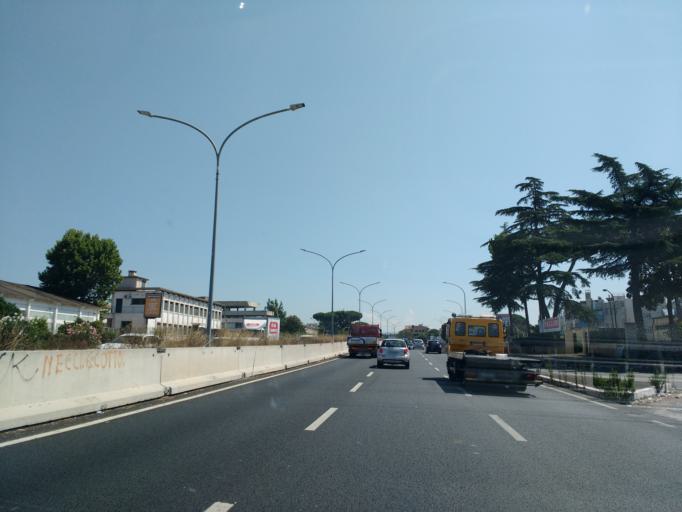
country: IT
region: Latium
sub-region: Citta metropolitana di Roma Capitale
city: Setteville
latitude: 41.9364
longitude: 12.6149
